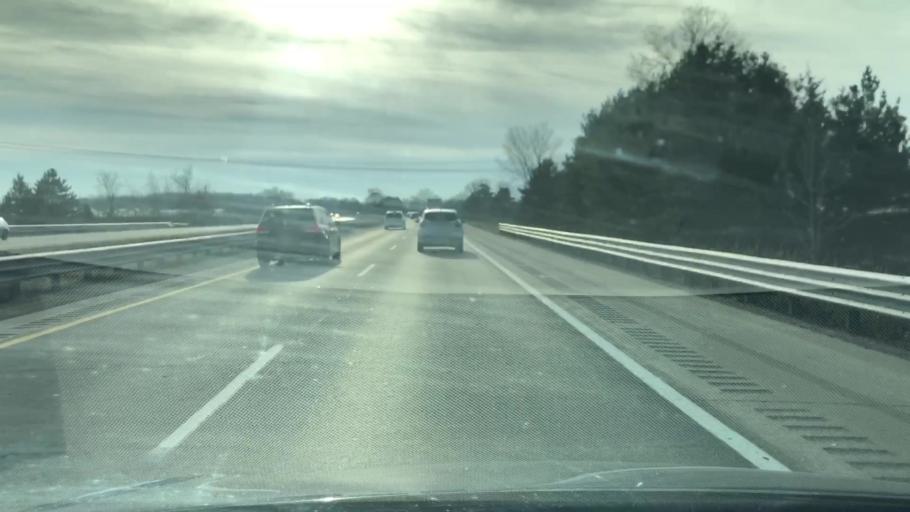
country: US
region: Michigan
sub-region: Genesee County
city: Lake Fenton
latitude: 42.9003
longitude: -83.7341
